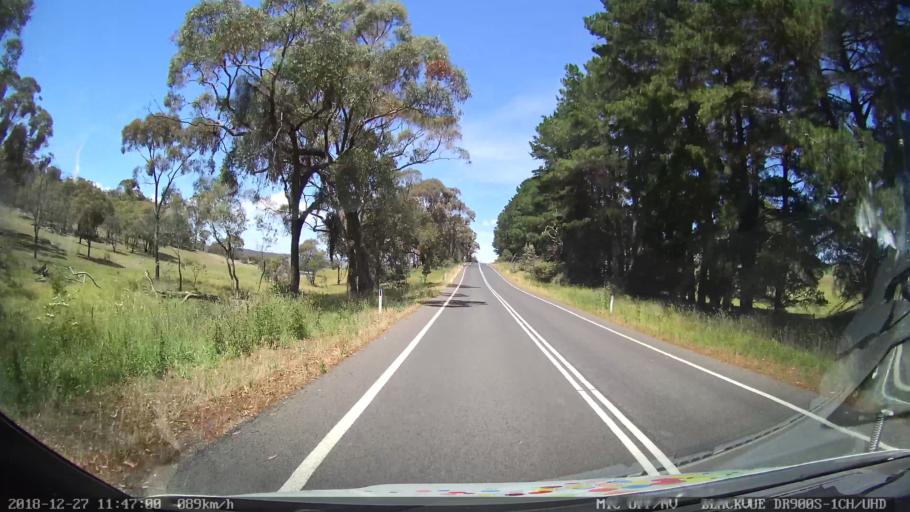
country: AU
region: New South Wales
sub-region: Bathurst Regional
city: Perthville
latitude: -33.5918
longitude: 149.4497
